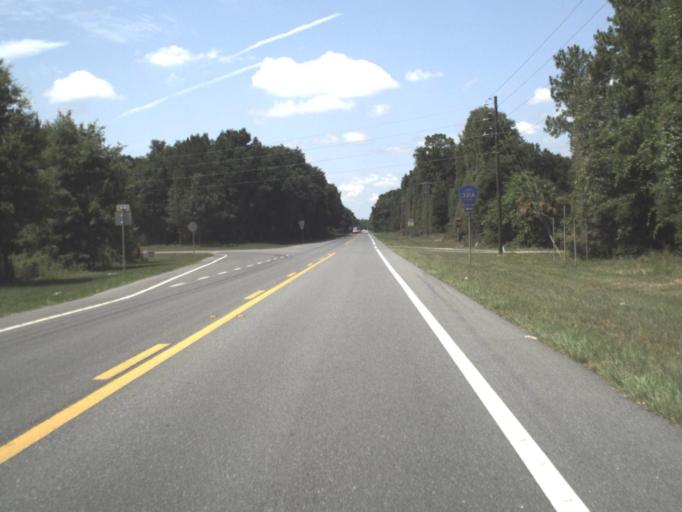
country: US
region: Florida
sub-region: Levy County
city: Williston
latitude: 29.4157
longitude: -82.4296
